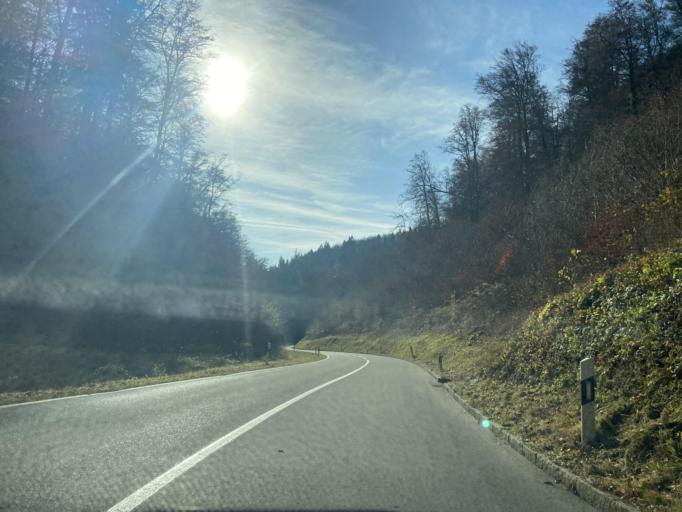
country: DE
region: Baden-Wuerttemberg
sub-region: Tuebingen Region
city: Stetten am Kalten Markt
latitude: 48.1023
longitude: 9.0943
